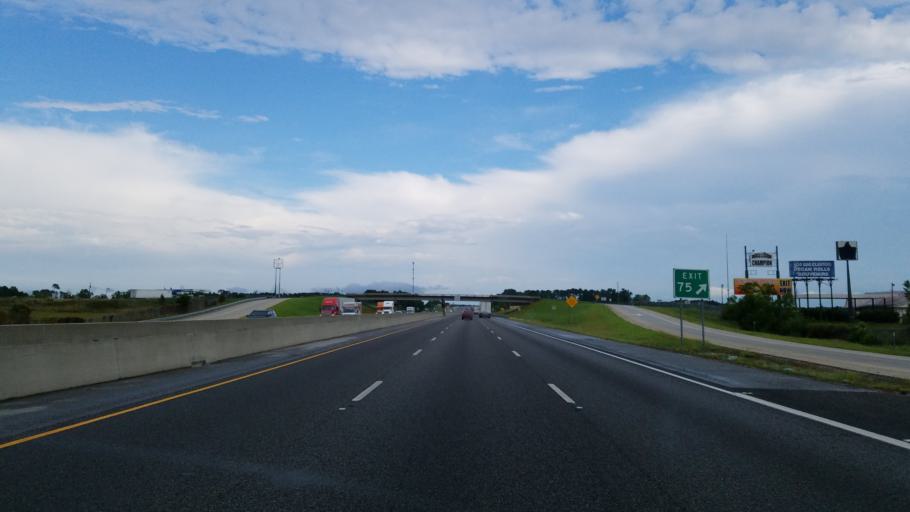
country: US
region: Georgia
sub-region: Turner County
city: Ashburn
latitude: 31.6287
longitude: -83.5782
